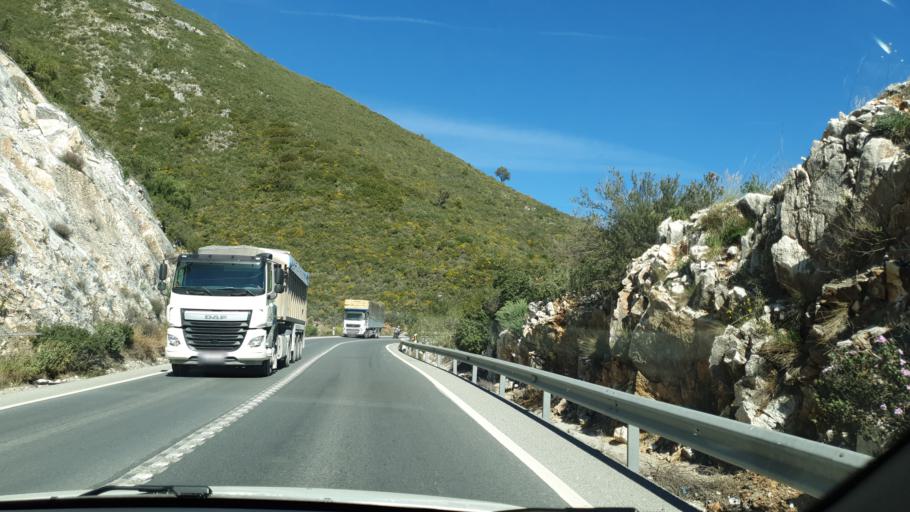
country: ES
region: Andalusia
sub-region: Provincia de Malaga
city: Ojen
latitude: 36.5790
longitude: -4.8530
